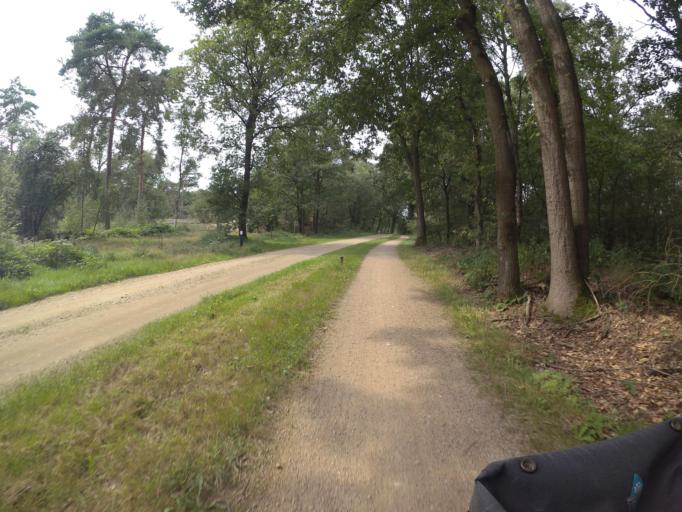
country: NL
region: Limburg
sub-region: Gemeente Bergen
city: Wellerlooi
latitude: 51.5556
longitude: 6.1433
